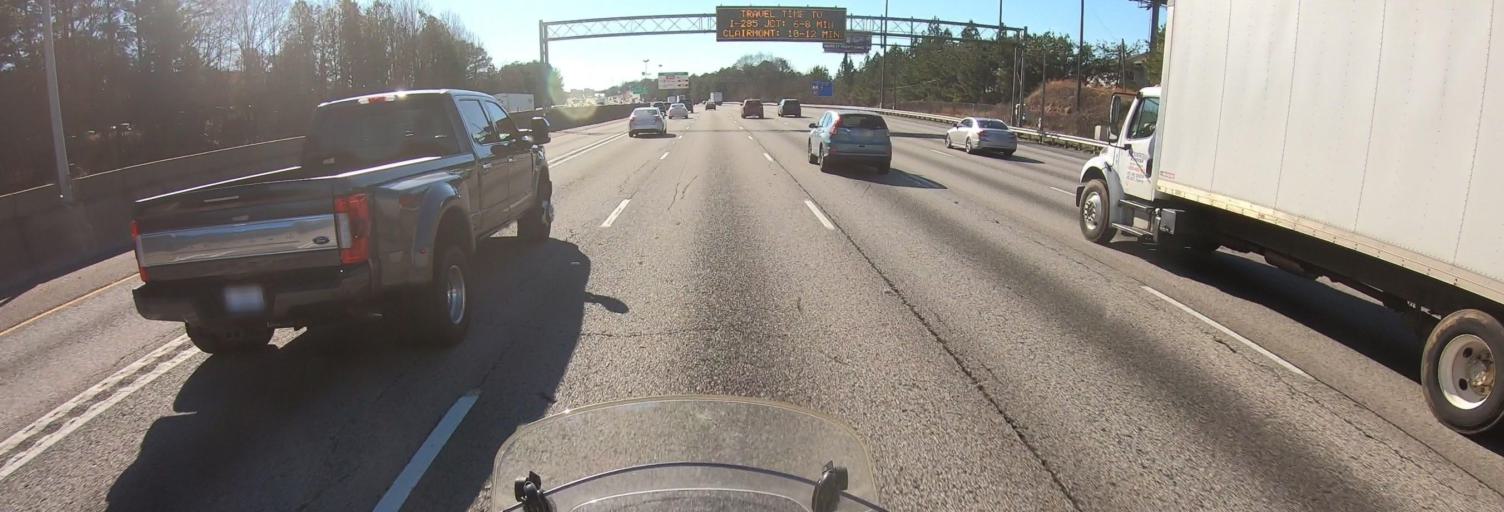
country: US
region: Georgia
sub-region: Gwinnett County
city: Lilburn
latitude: 33.9427
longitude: -84.1514
